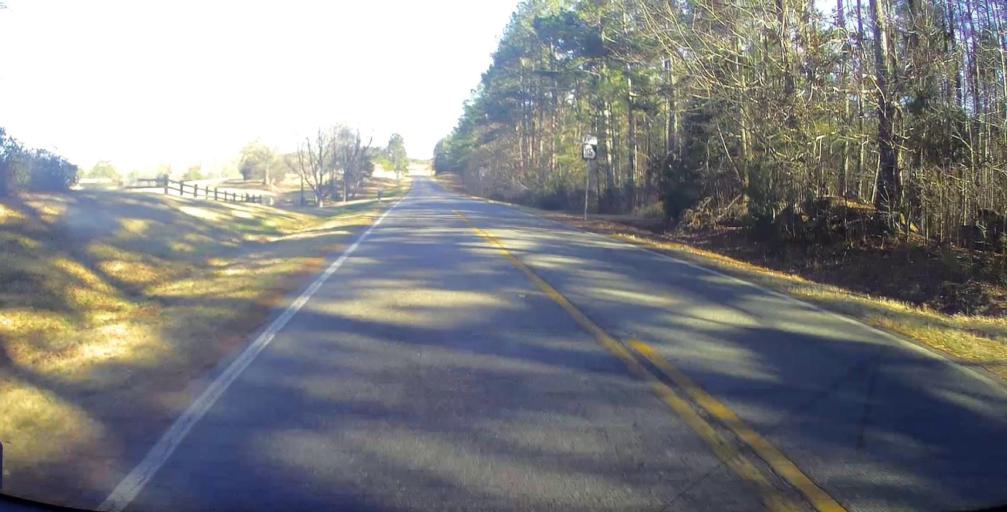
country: US
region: Georgia
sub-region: Talbot County
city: Sardis
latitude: 32.7879
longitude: -84.6441
